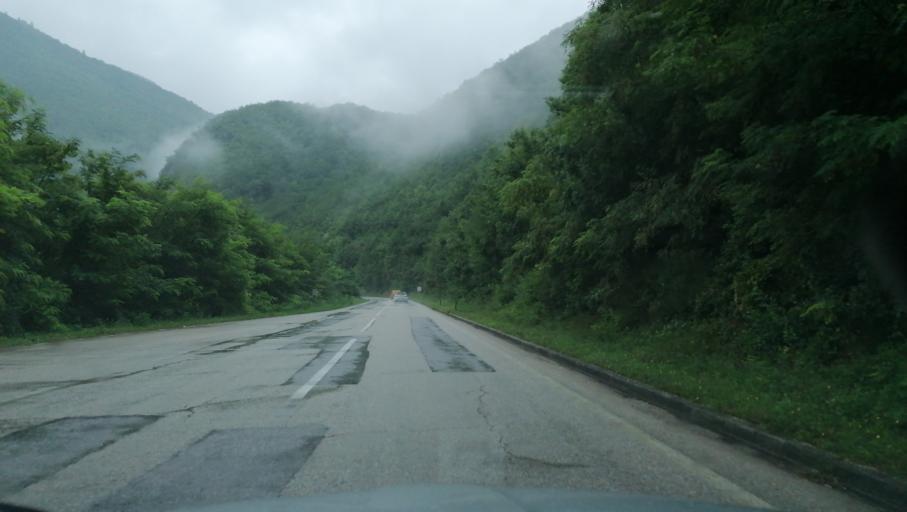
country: BA
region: Republika Srpska
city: Cajnice
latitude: 43.6844
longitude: 19.1513
